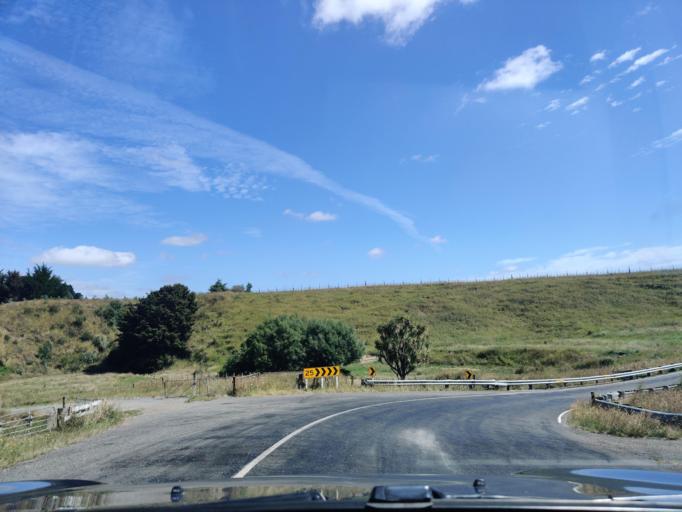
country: NZ
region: Manawatu-Wanganui
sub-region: Rangitikei District
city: Bulls
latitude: -40.1709
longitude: 175.4324
